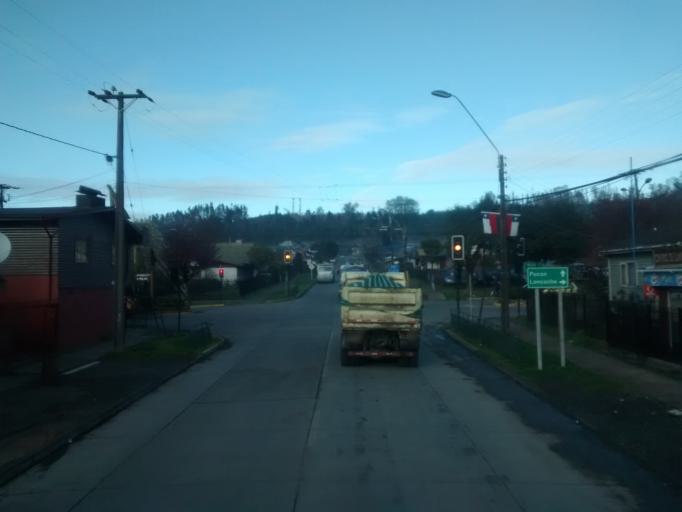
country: CL
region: Araucania
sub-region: Provincia de Cautin
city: Villarrica
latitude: -39.2789
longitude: -72.2330
